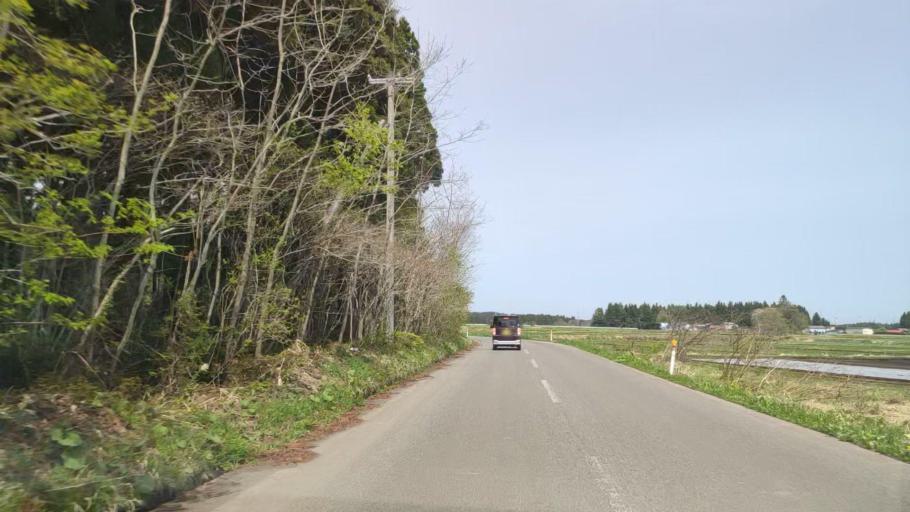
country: JP
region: Aomori
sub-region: Misawa Shi
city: Inuotose
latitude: 40.7691
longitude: 141.1222
